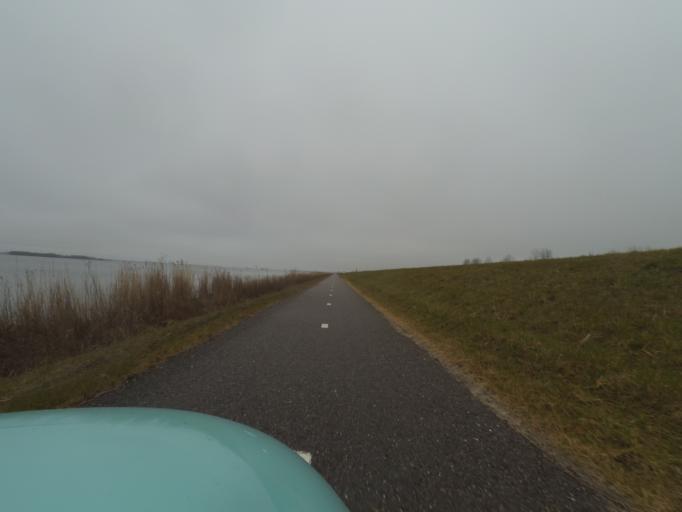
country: NL
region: Flevoland
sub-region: Gemeente Dronten
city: Biddinghuizen
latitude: 52.4103
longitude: 5.7019
